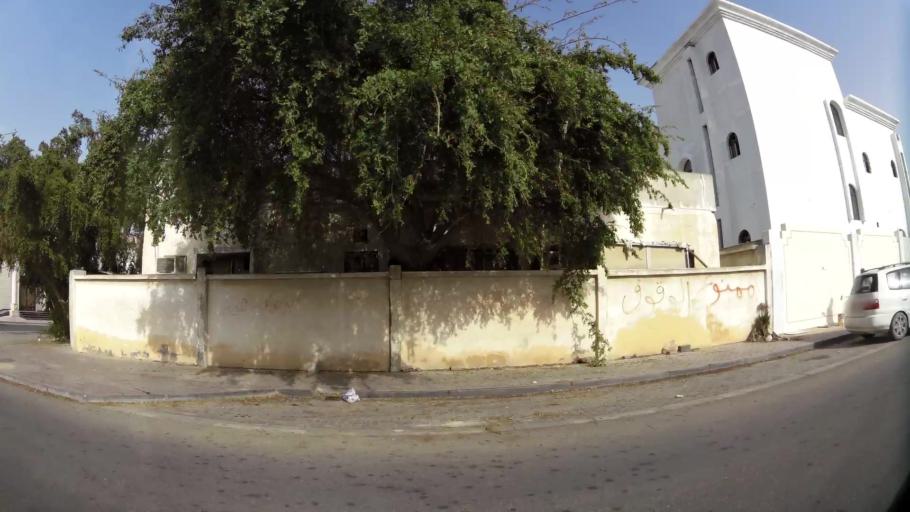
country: QA
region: Baladiyat ar Rayyan
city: Ar Rayyan
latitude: 25.2394
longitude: 51.4364
